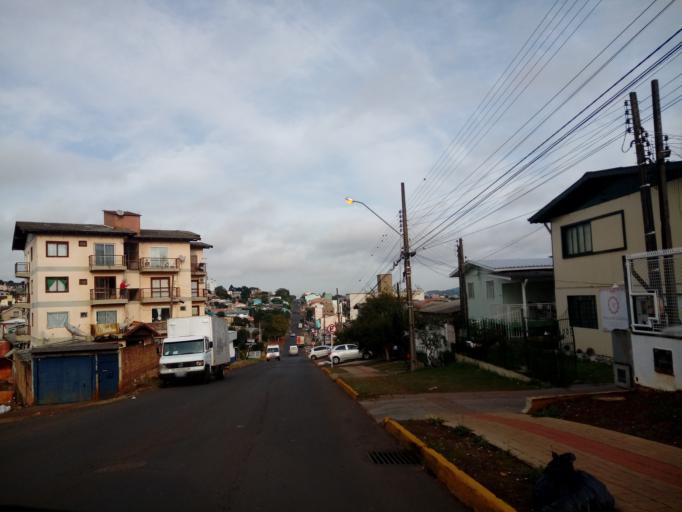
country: BR
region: Santa Catarina
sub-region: Chapeco
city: Chapeco
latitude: -27.0717
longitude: -52.6288
